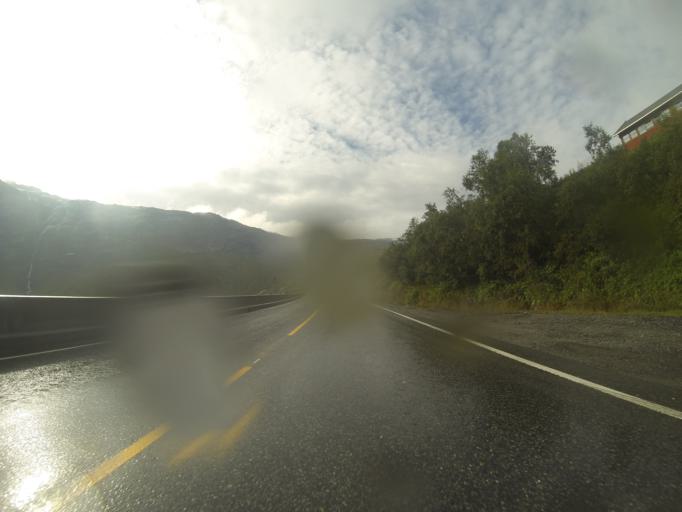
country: NO
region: Hordaland
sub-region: Odda
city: Odda
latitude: 59.8216
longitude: 6.7452
